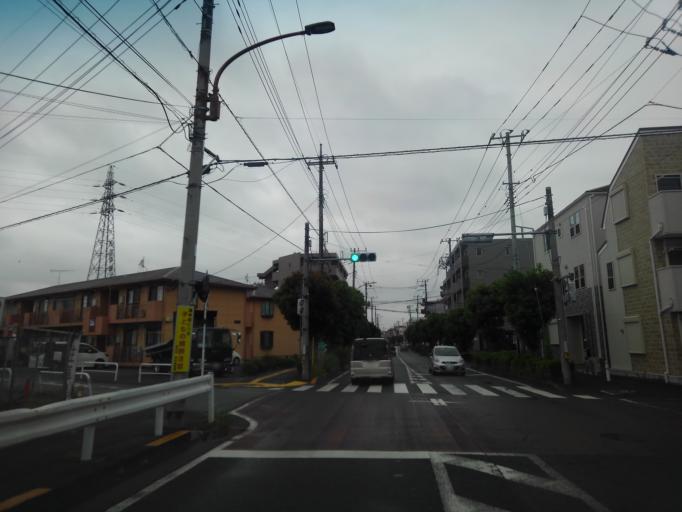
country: JP
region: Tokyo
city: Chofugaoka
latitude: 35.6599
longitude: 139.5018
